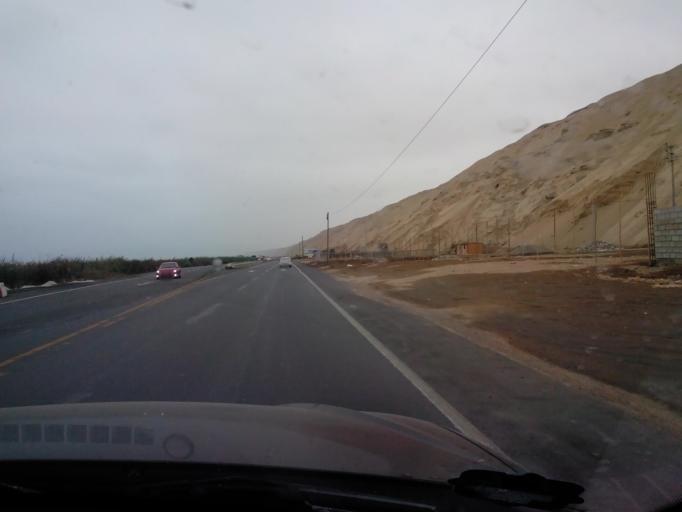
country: PE
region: Ica
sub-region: Provincia de Chincha
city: San Pedro
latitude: -13.4037
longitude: -76.1936
